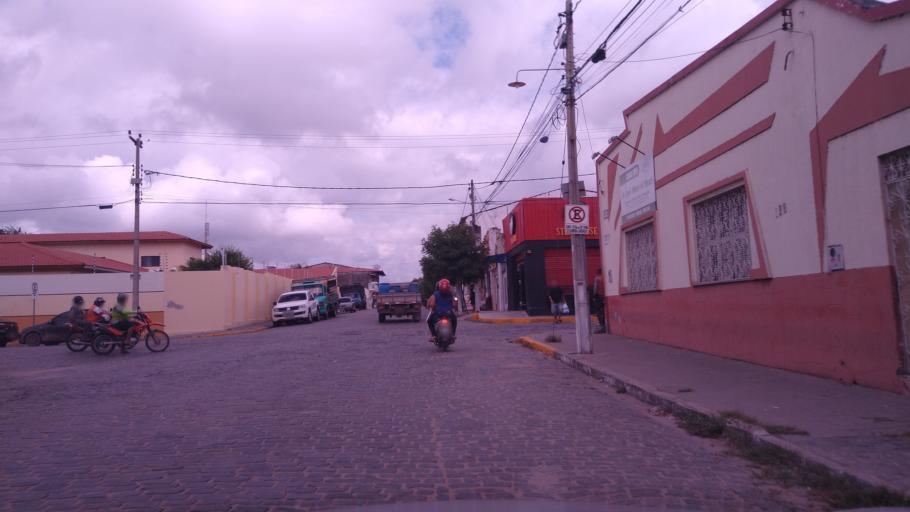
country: BR
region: Ceara
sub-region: Quixada
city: Quixada
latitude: -4.9670
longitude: -39.0171
